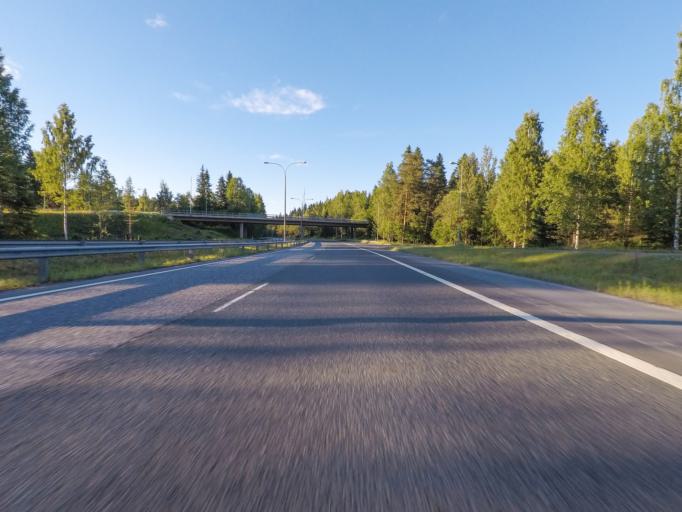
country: FI
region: Northern Savo
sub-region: Kuopio
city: Kuopio
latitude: 62.9033
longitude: 27.6817
